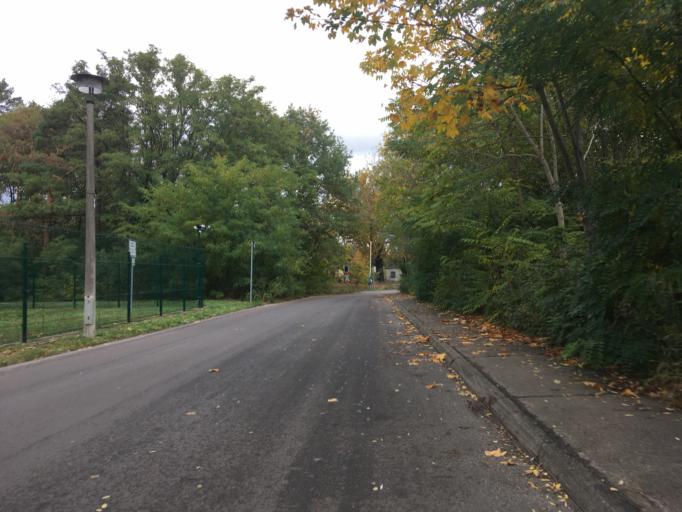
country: DE
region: Berlin
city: Adlershof
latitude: 52.4505
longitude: 13.5546
